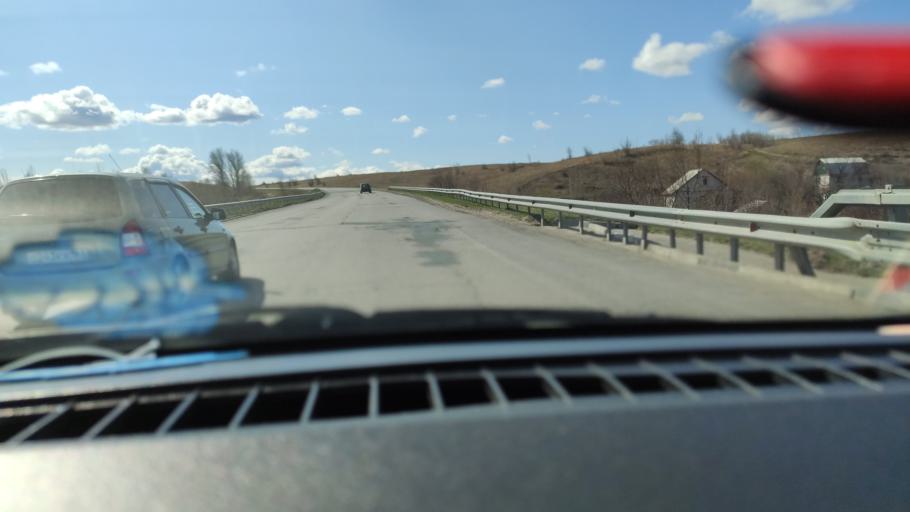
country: RU
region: Samara
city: Varlamovo
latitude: 53.1264
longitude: 48.2911
